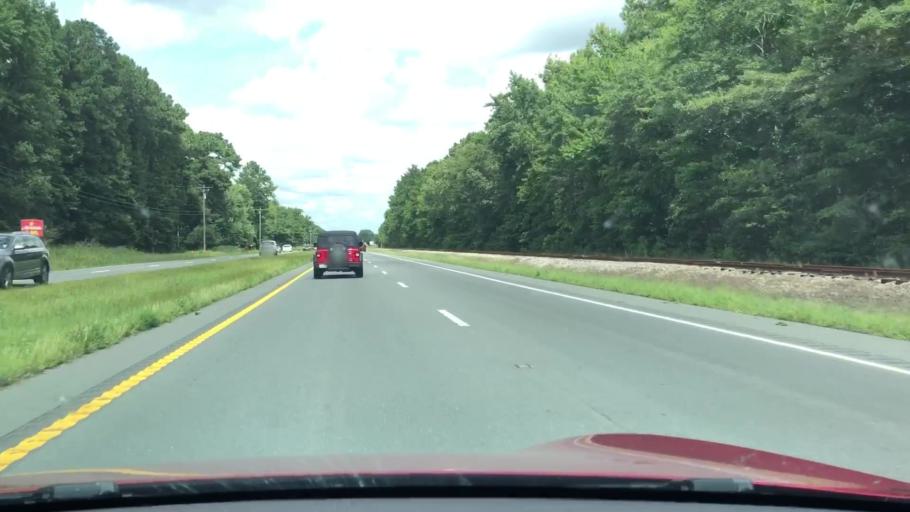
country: US
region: Virginia
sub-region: Accomack County
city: Onancock
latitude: 37.6291
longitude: -75.7563
